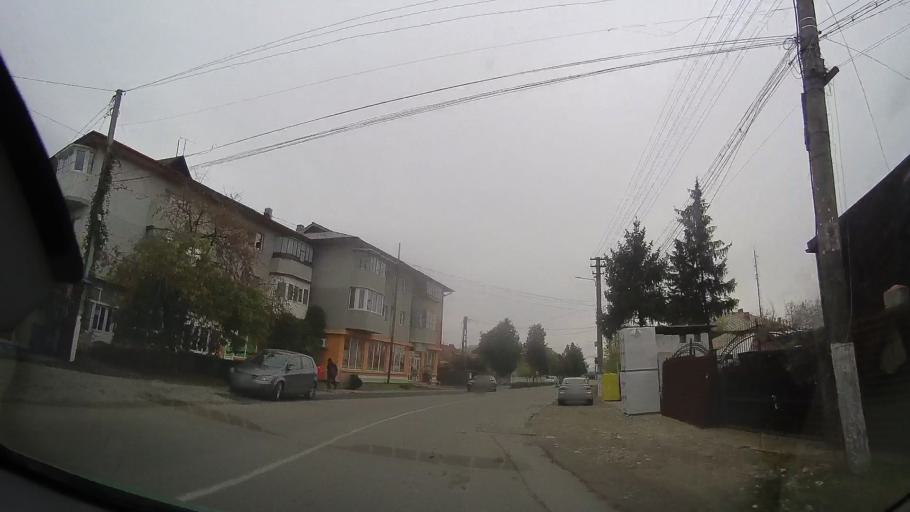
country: RO
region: Prahova
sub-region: Comuna Ceptura
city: Ceptura de Jos
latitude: 45.0181
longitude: 26.3281
